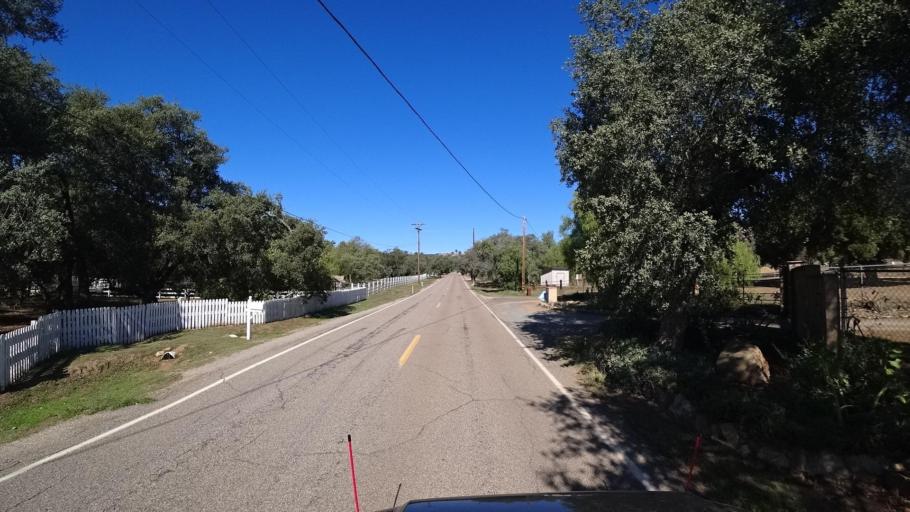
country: US
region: California
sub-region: San Diego County
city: Jamul
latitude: 32.7247
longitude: -116.8141
